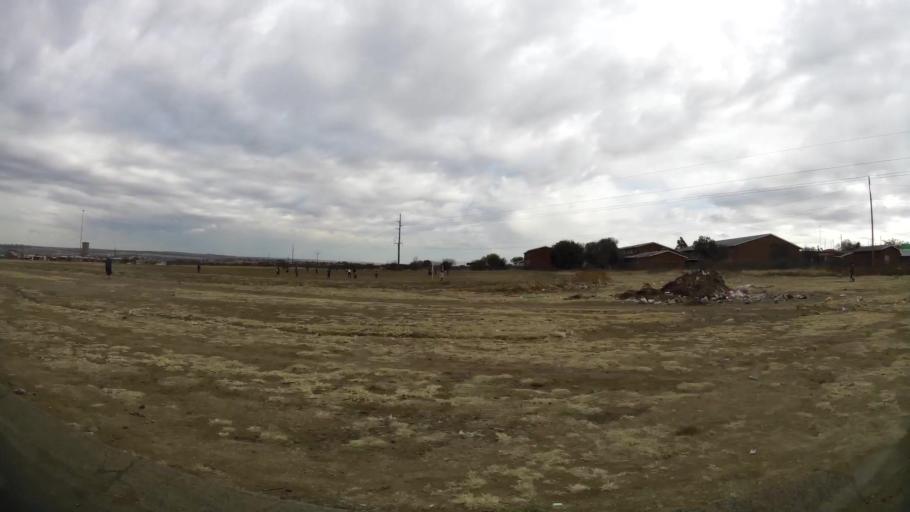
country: ZA
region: Orange Free State
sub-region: Fezile Dabi District Municipality
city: Kroonstad
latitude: -27.6544
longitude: 27.2007
